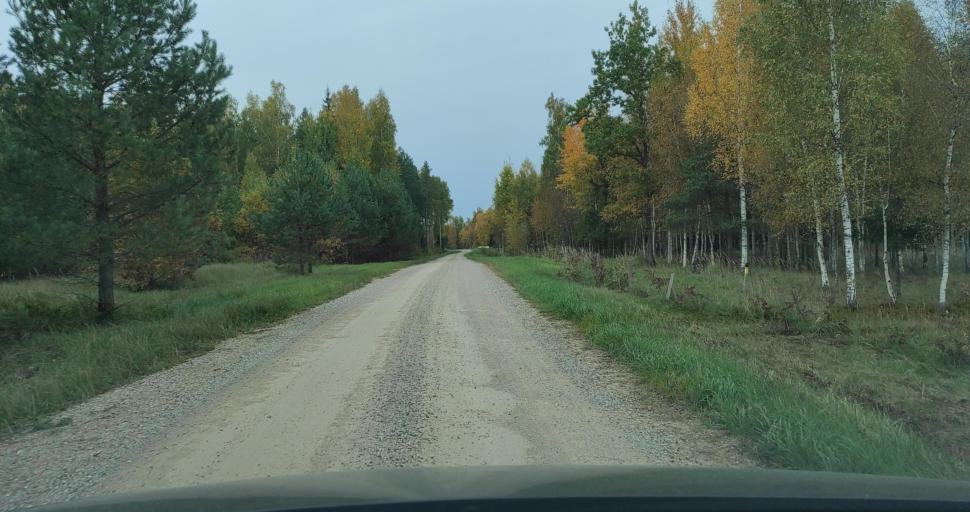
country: LV
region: Kuldigas Rajons
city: Kuldiga
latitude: 57.0237
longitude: 22.2000
